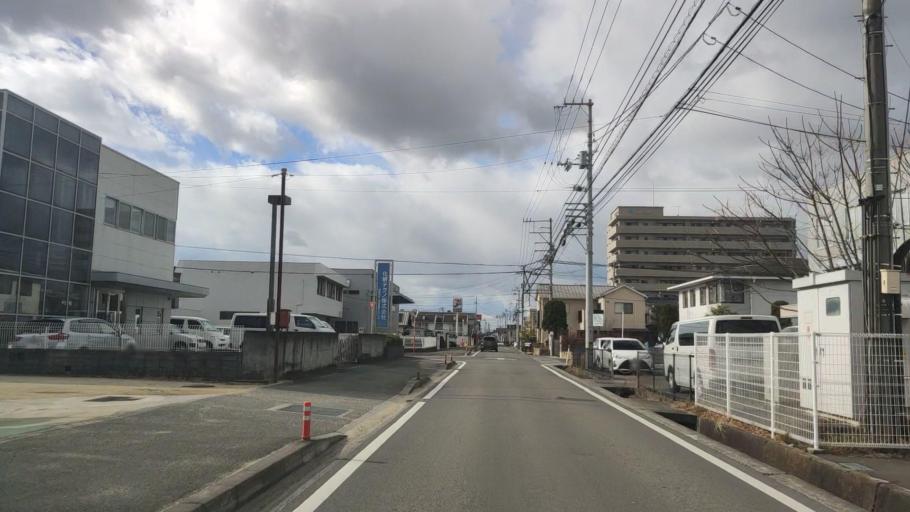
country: JP
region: Ehime
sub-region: Shikoku-chuo Shi
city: Matsuyama
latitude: 33.8098
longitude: 132.7945
